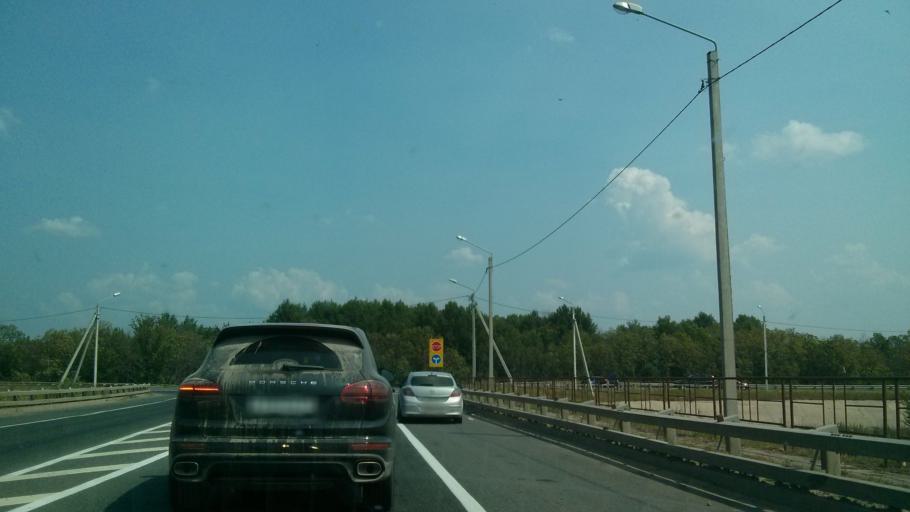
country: RU
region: Nizjnij Novgorod
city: Navashino
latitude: 55.5864
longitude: 42.1483
